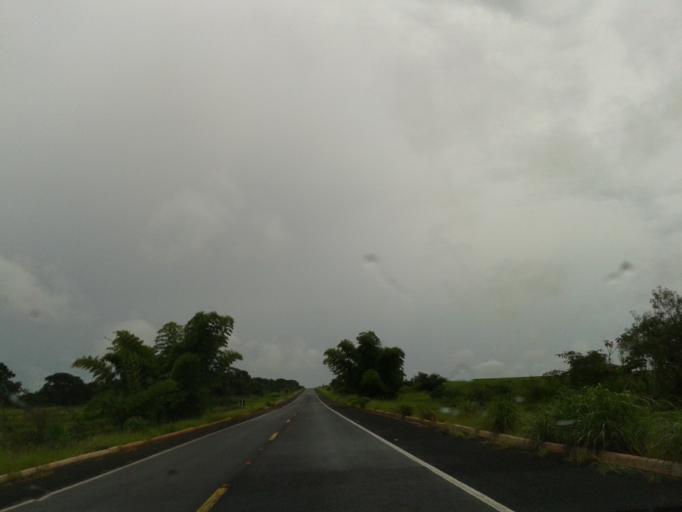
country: BR
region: Minas Gerais
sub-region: Santa Vitoria
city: Santa Vitoria
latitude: -19.1502
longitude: -50.1554
